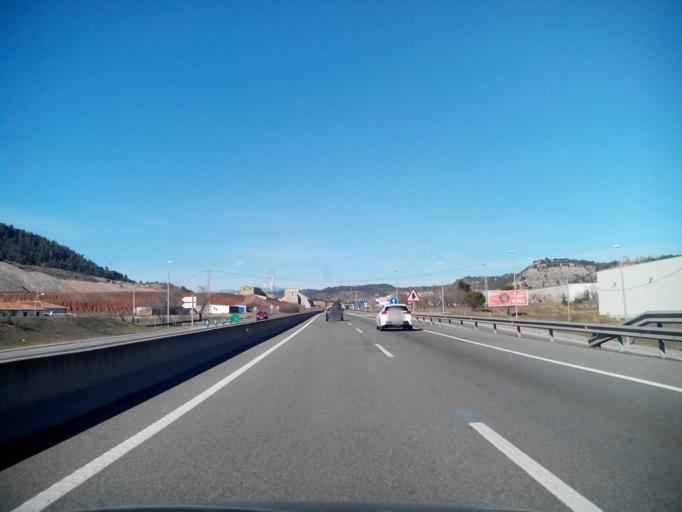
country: ES
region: Catalonia
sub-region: Provincia de Barcelona
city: Sallent
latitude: 41.8050
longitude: 1.8978
